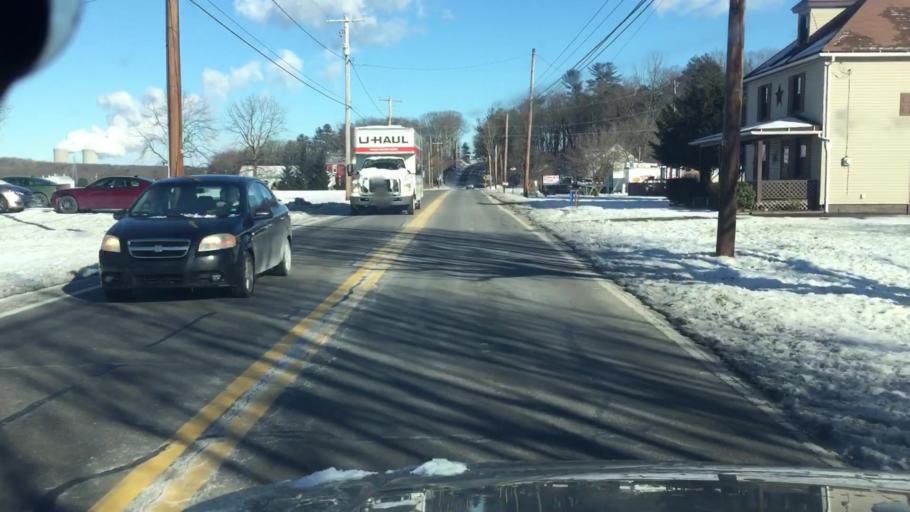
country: US
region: Pennsylvania
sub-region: Luzerne County
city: Nescopeck
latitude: 41.0538
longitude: -76.2061
